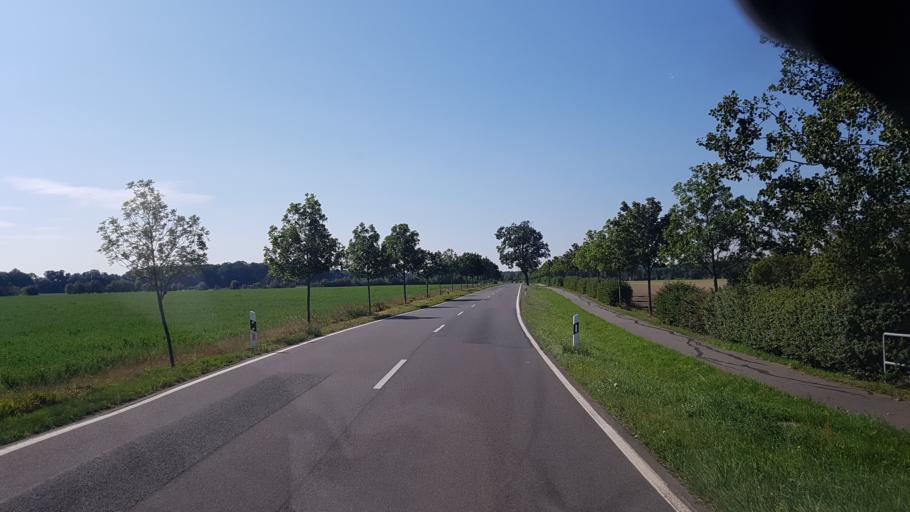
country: DE
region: Brandenburg
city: Vetschau
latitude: 51.7231
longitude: 14.0434
